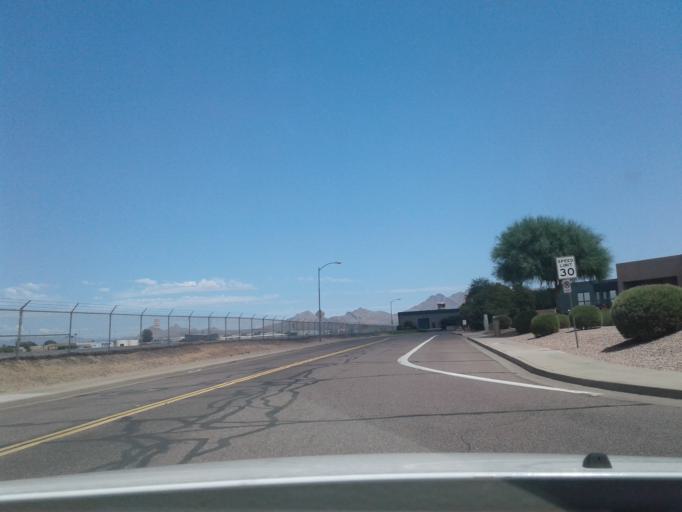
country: US
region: Arizona
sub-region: Maricopa County
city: Paradise Valley
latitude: 33.6168
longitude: -111.9158
